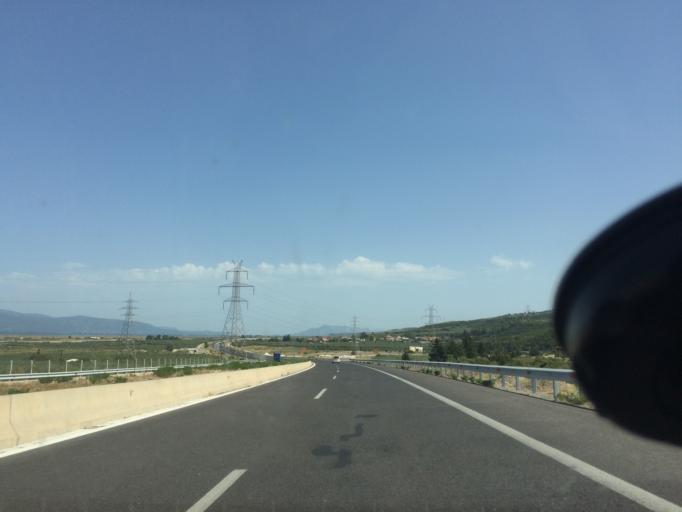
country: GR
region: Central Greece
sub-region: Nomos Fthiotidos
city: Anthili
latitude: 38.7972
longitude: 22.5269
